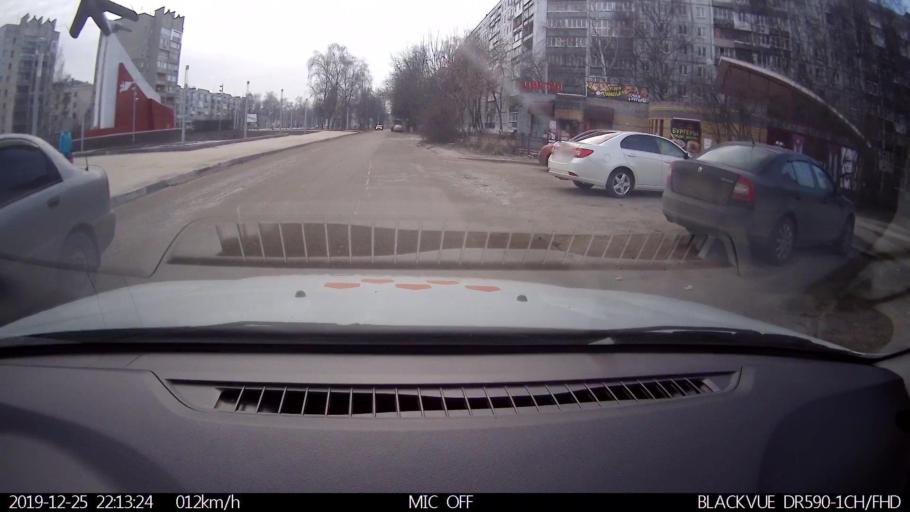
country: RU
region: Nizjnij Novgorod
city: Gorbatovka
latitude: 56.3346
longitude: 43.8479
